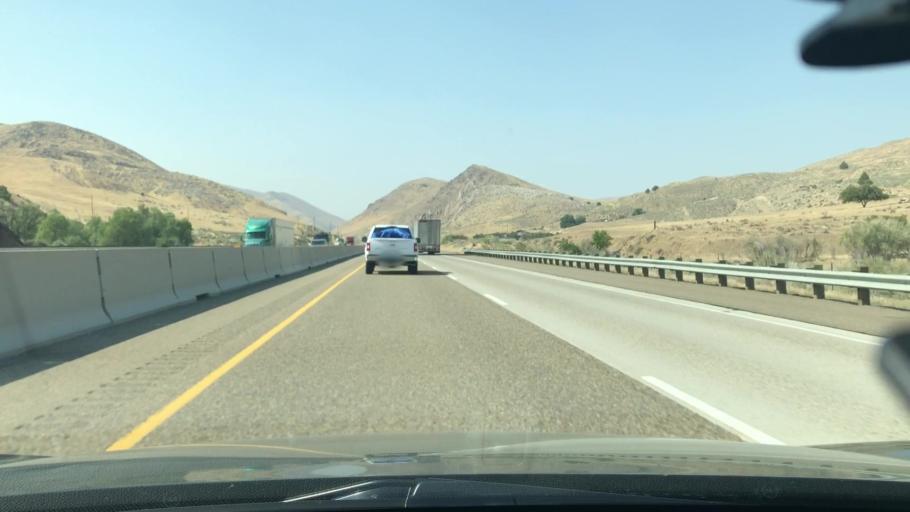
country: US
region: Idaho
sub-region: Washington County
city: Weiser
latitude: 44.4188
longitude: -117.3098
